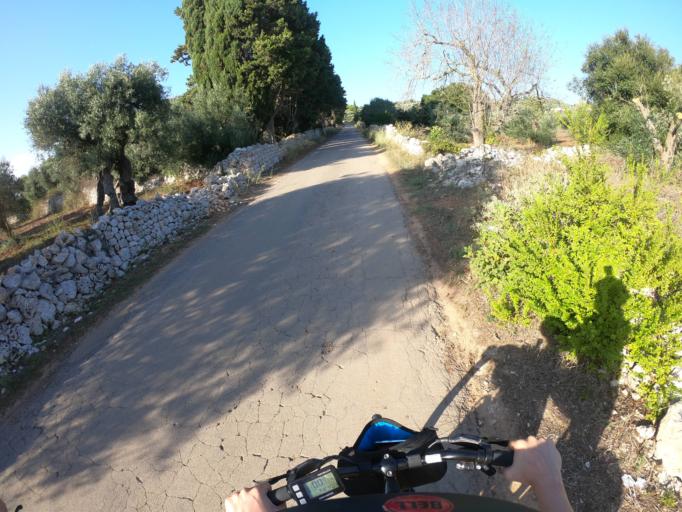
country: IT
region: Apulia
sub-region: Provincia di Lecce
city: Castrignano del Capo
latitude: 39.8248
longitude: 18.3568
